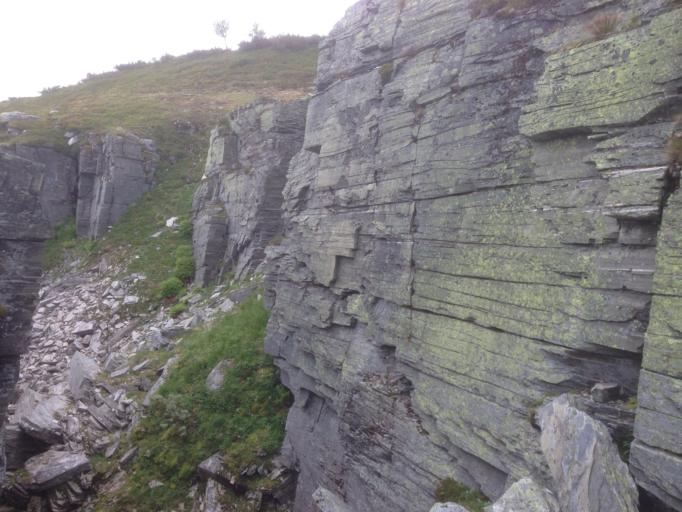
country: SE
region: Jaemtland
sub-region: Are Kommun
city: Are
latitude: 62.6953
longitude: 12.9420
